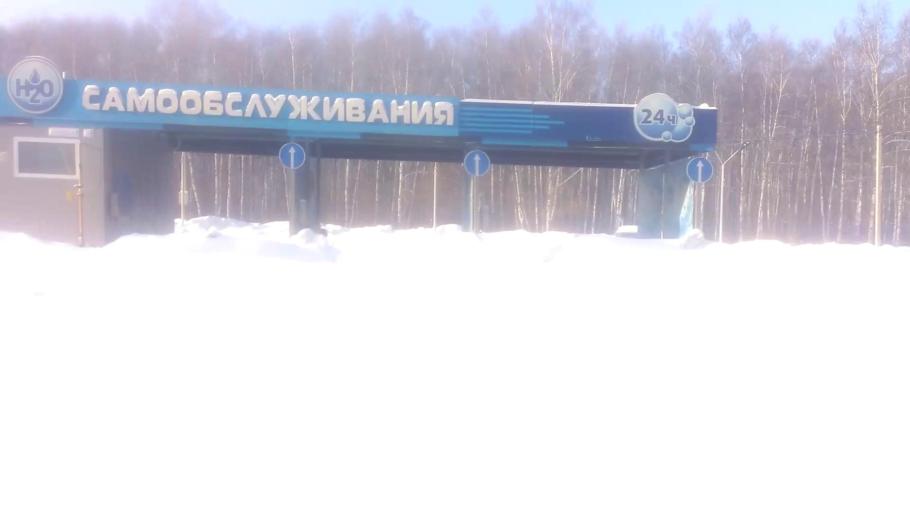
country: RU
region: Altai Krai
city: Novosilikatnyy
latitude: 53.3714
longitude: 83.6622
